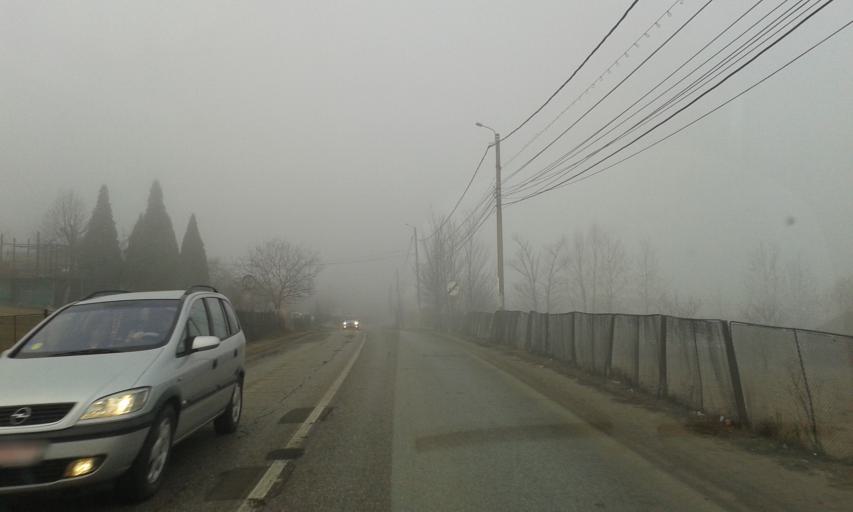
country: RO
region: Hunedoara
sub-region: Comuna Aninoasa
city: Iscroni
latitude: 45.3775
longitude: 23.3170
